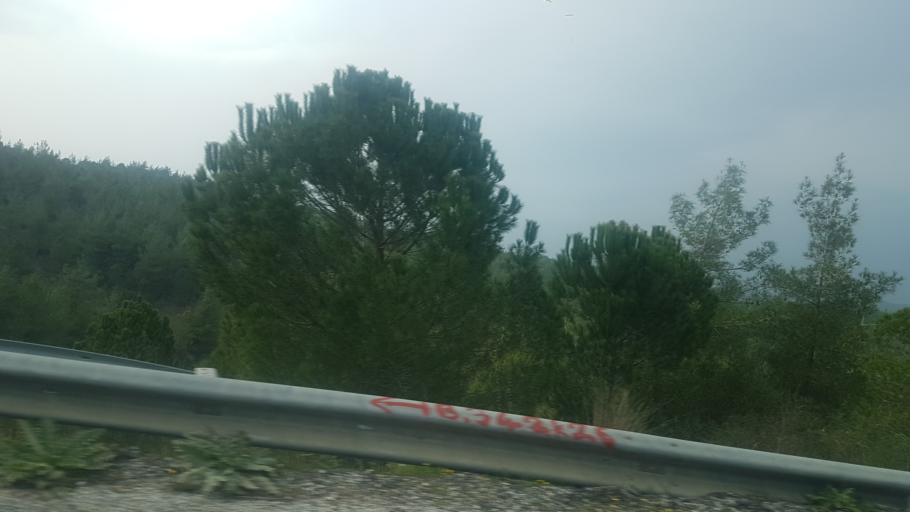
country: TR
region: Mersin
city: Yenice
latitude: 37.0755
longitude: 35.1694
